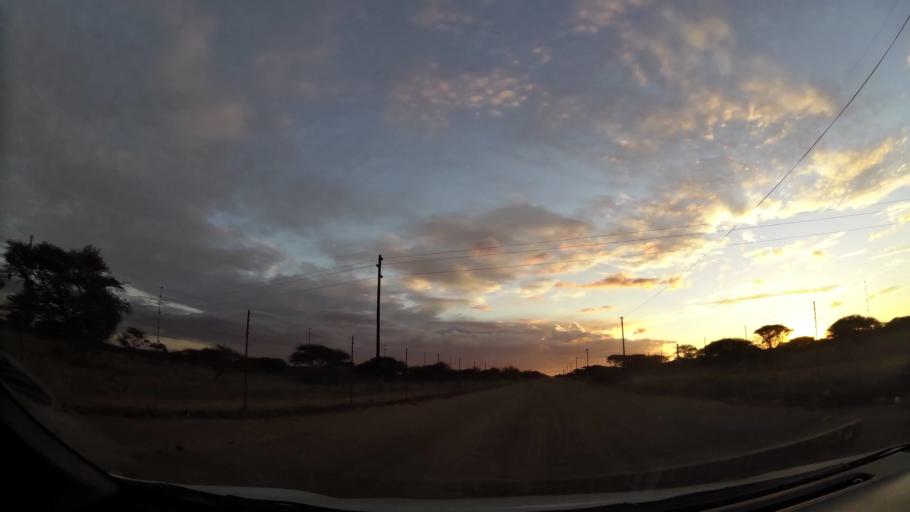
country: ZA
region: Limpopo
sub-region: Capricorn District Municipality
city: Polokwane
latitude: -23.7435
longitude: 29.4687
